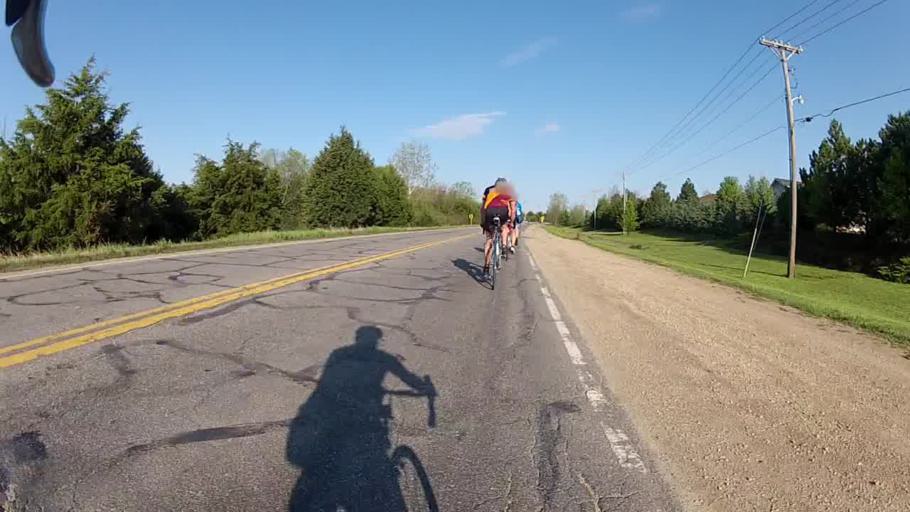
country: US
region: Kansas
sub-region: Riley County
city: Manhattan
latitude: 39.1887
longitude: -96.6337
